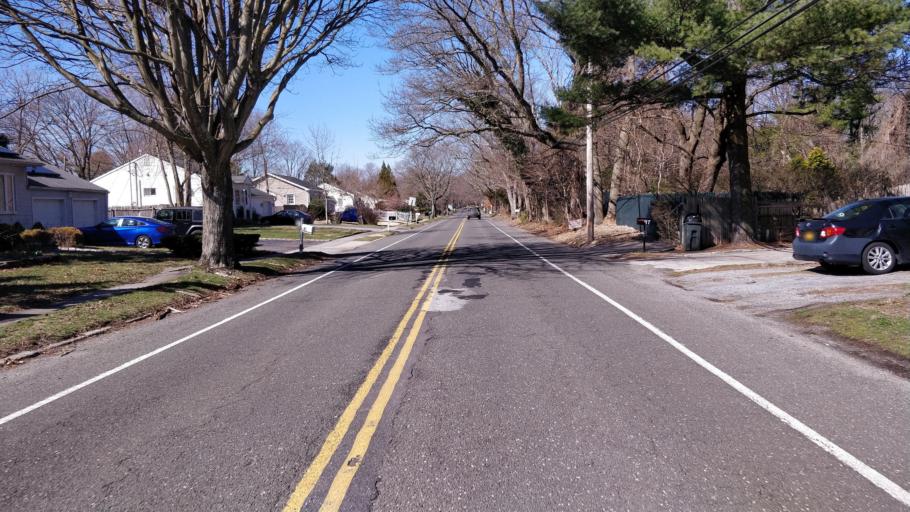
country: US
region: New York
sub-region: Suffolk County
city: Greenlawn
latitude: 40.8513
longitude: -73.3703
